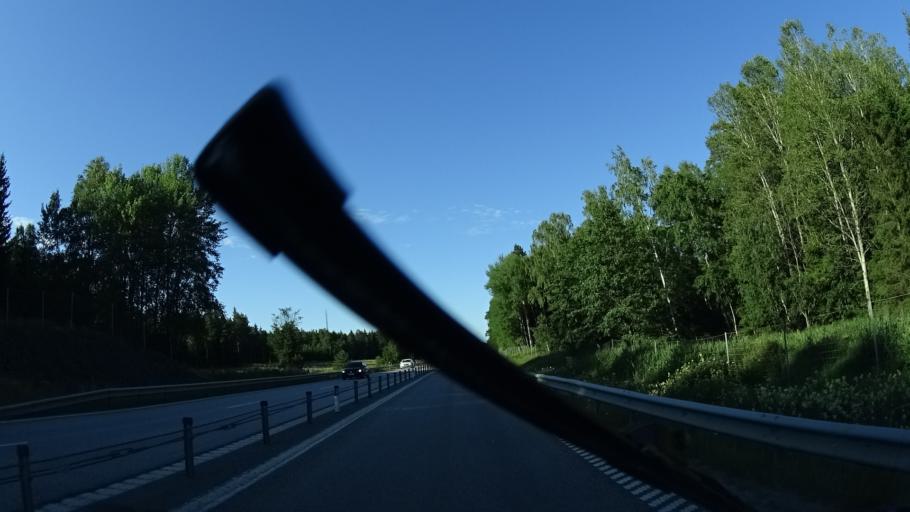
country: SE
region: Stockholm
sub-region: Vallentuna Kommun
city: Vallentuna
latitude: 59.5198
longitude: 18.1813
